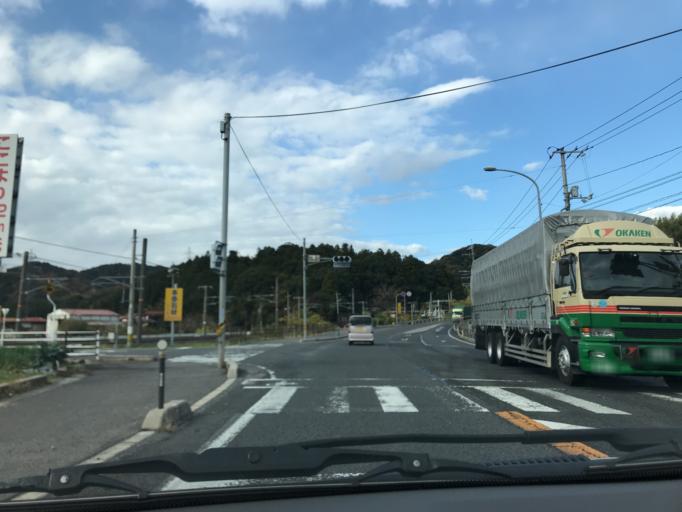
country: JP
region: Tottori
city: Yonago
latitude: 35.4082
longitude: 133.2997
